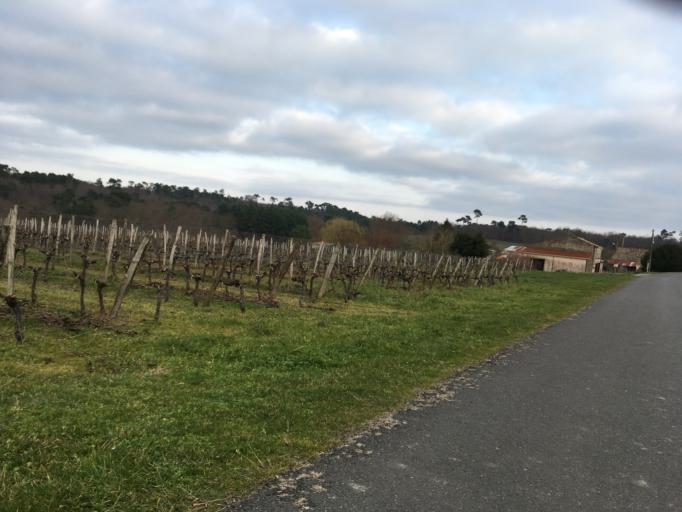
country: FR
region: Aquitaine
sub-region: Departement de la Gironde
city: Saint-Ciers-sur-Gironde
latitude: 45.3146
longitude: -0.6152
